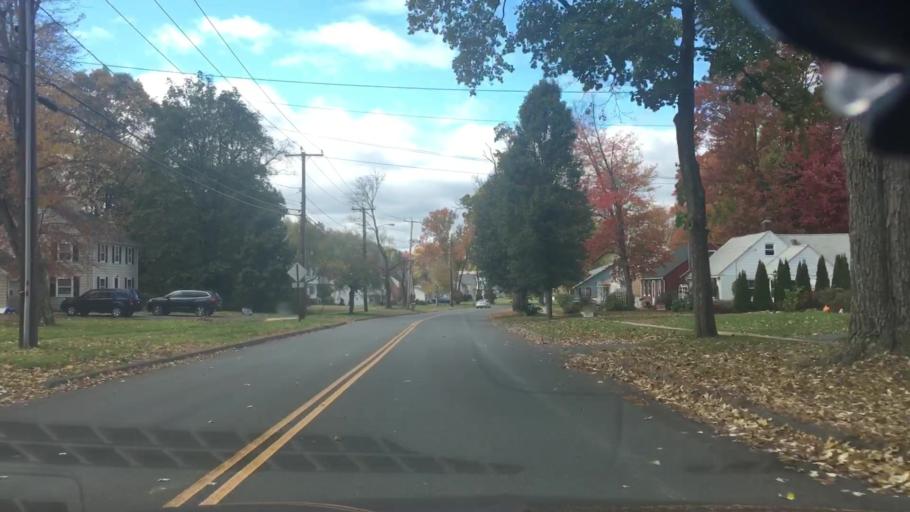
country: US
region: Massachusetts
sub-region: Hampden County
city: Longmeadow
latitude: 42.0320
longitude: -72.5752
